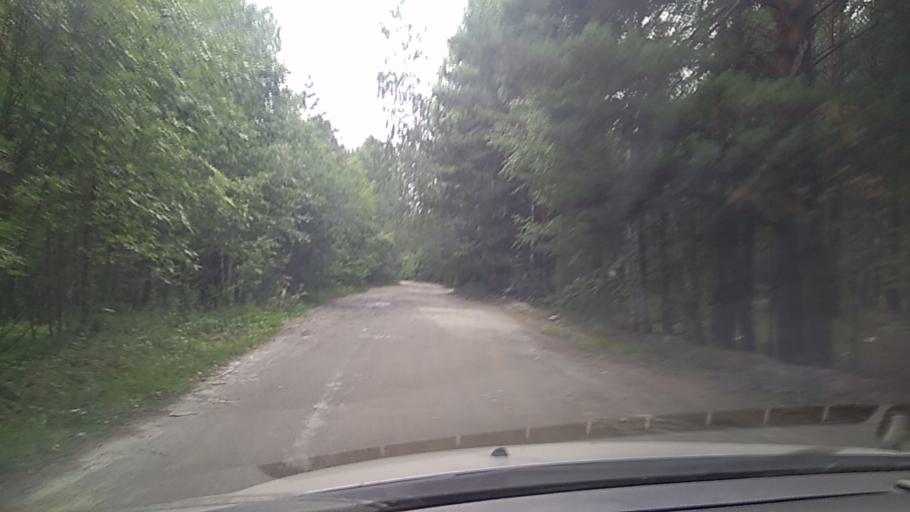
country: RU
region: Chelyabinsk
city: Kyshtym
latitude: 55.6784
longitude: 60.5837
